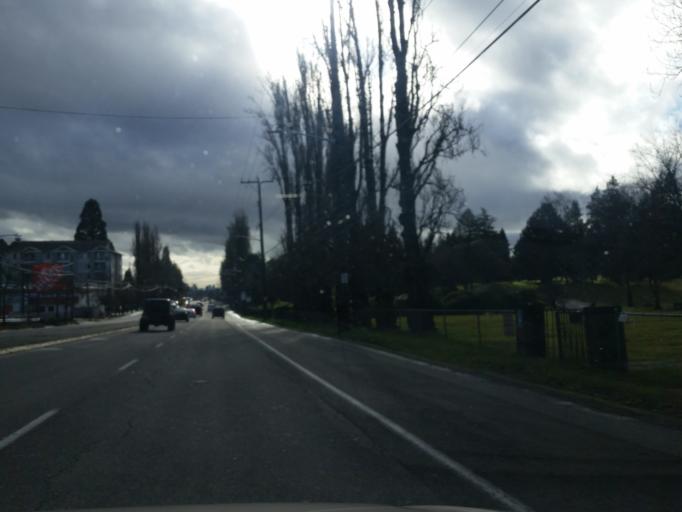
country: US
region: Washington
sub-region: King County
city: Shoreline
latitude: 47.7144
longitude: -122.3450
